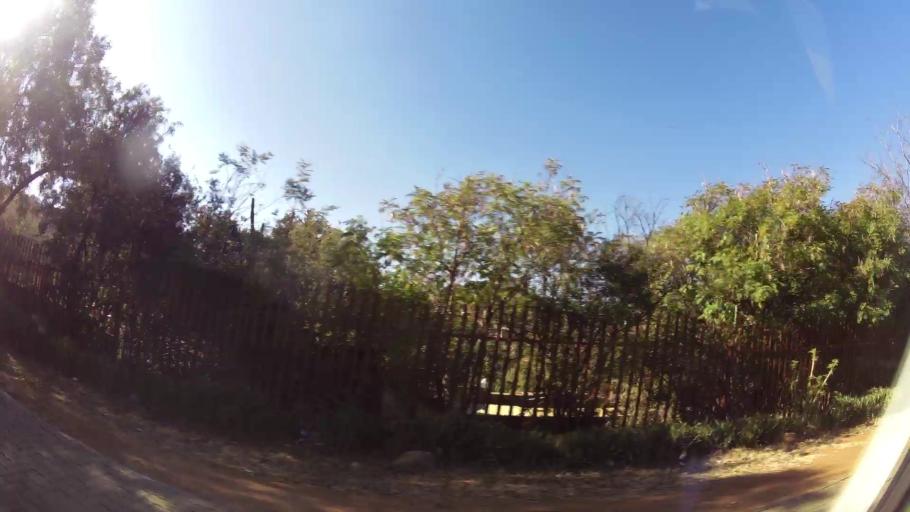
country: ZA
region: Gauteng
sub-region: City of Johannesburg Metropolitan Municipality
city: Johannesburg
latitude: -26.2782
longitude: 28.0521
